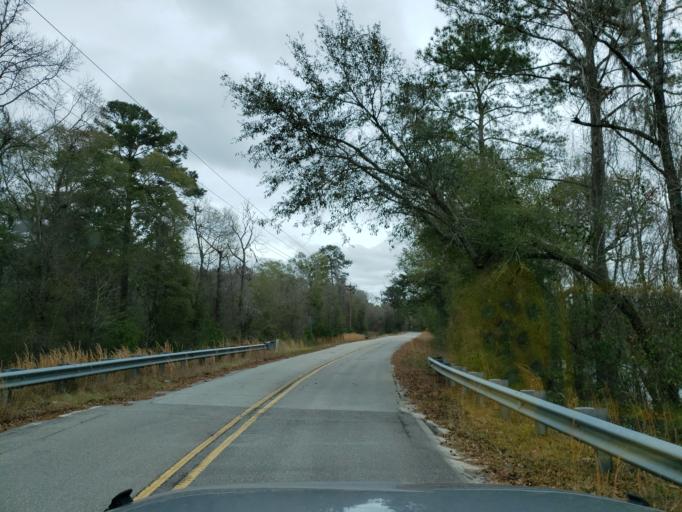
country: US
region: Georgia
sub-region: Chatham County
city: Bloomingdale
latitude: 32.0839
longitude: -81.3816
